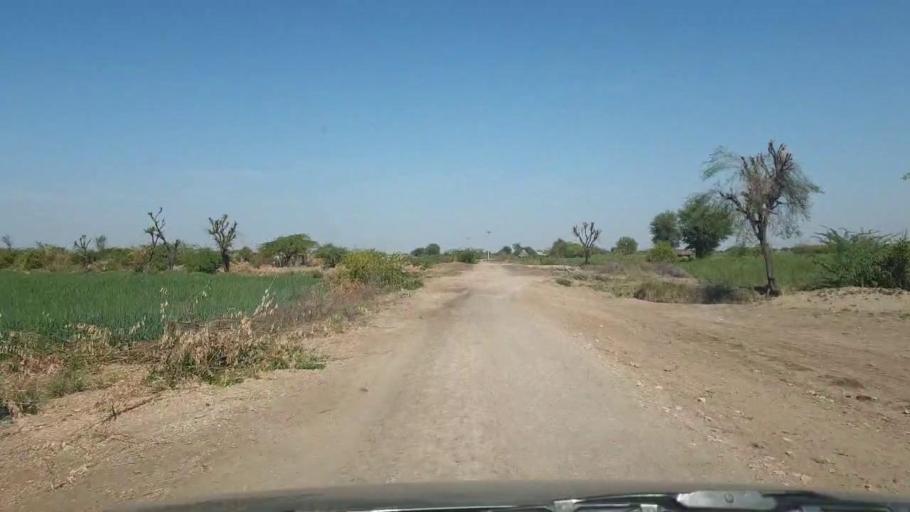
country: PK
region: Sindh
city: Dhoro Naro
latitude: 25.4125
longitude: 69.6172
